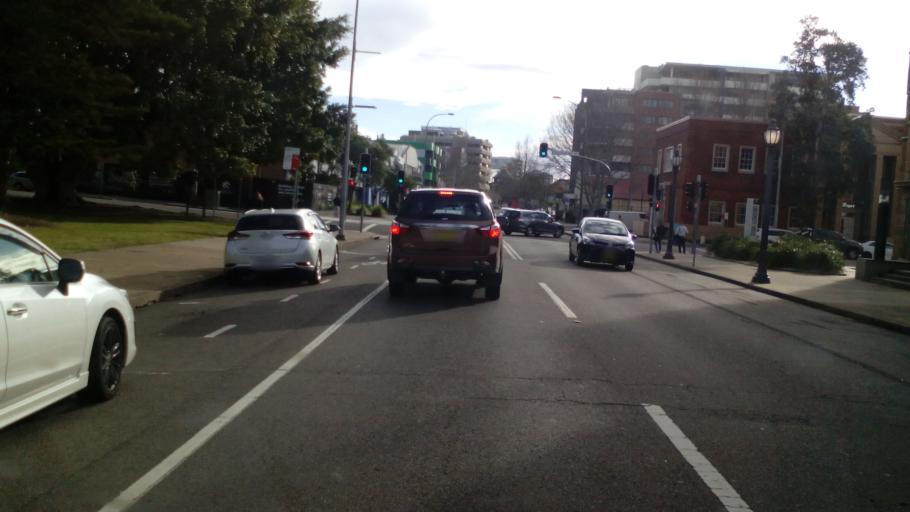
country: AU
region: New South Wales
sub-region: Newcastle
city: Cooks Hill
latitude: -32.9282
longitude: 151.7716
